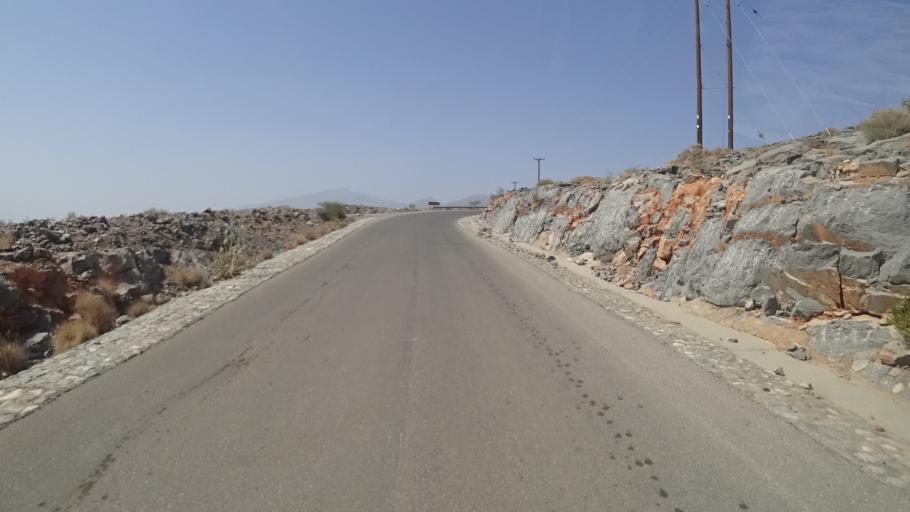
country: OM
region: Muhafazat ad Dakhiliyah
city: Bahla'
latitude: 23.1137
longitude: 57.4061
